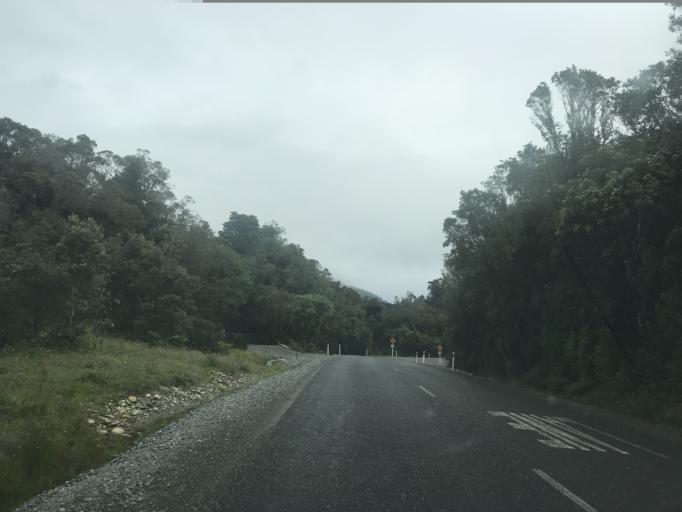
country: NZ
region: West Coast
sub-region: Westland District
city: Hokitika
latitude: -42.9540
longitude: 171.0227
